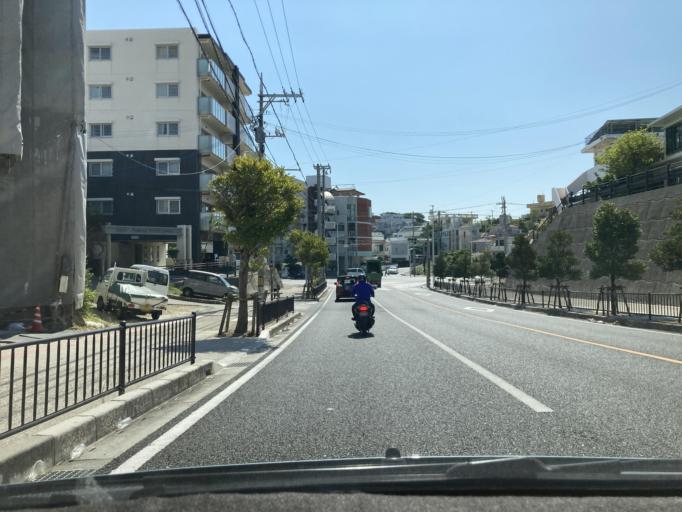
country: JP
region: Okinawa
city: Naha-shi
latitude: 26.2285
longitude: 127.7190
